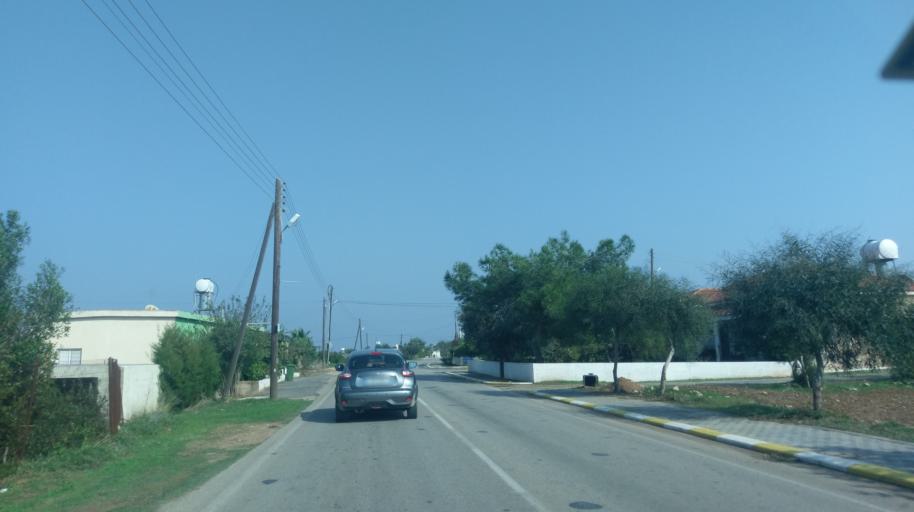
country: CY
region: Ammochostos
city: Leonarisso
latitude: 35.5267
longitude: 34.1805
